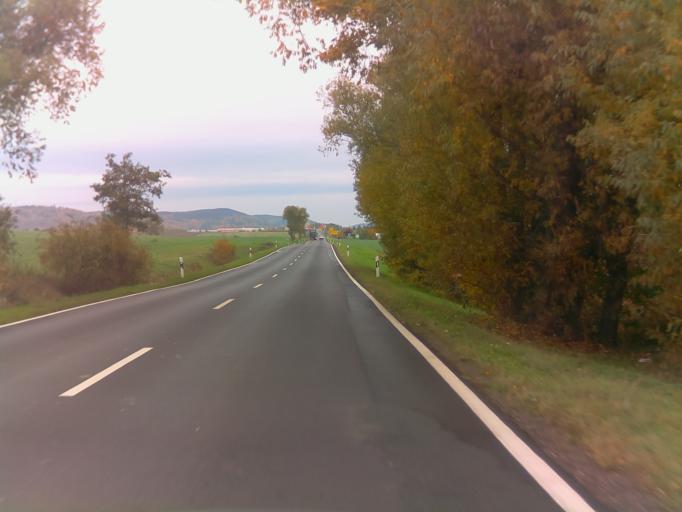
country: DE
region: Thuringia
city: Dornheim
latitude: 50.8254
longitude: 10.9956
